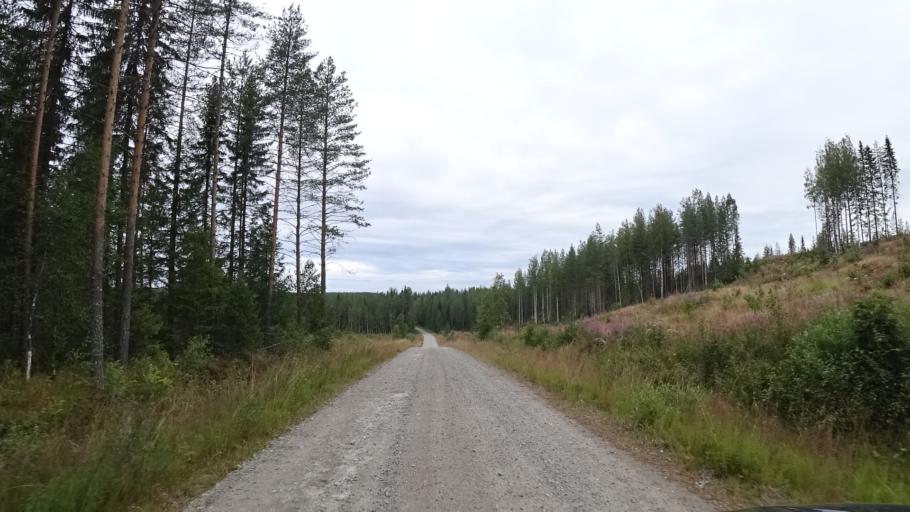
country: FI
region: North Karelia
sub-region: Joensuu
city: Ilomantsi
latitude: 63.1524
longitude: 30.6446
